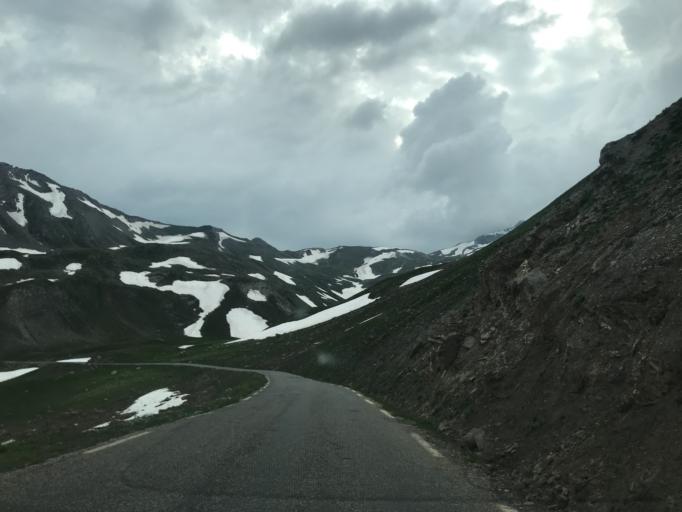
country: FR
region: Rhone-Alpes
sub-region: Departement de la Savoie
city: Valloire
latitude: 45.0534
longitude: 6.3983
